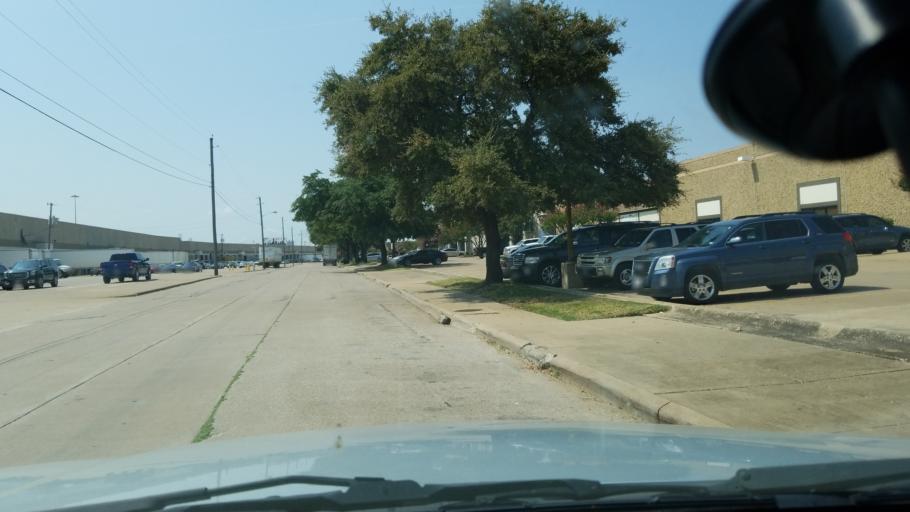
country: US
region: Texas
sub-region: Dallas County
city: Farmers Branch
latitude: 32.8709
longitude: -96.9002
